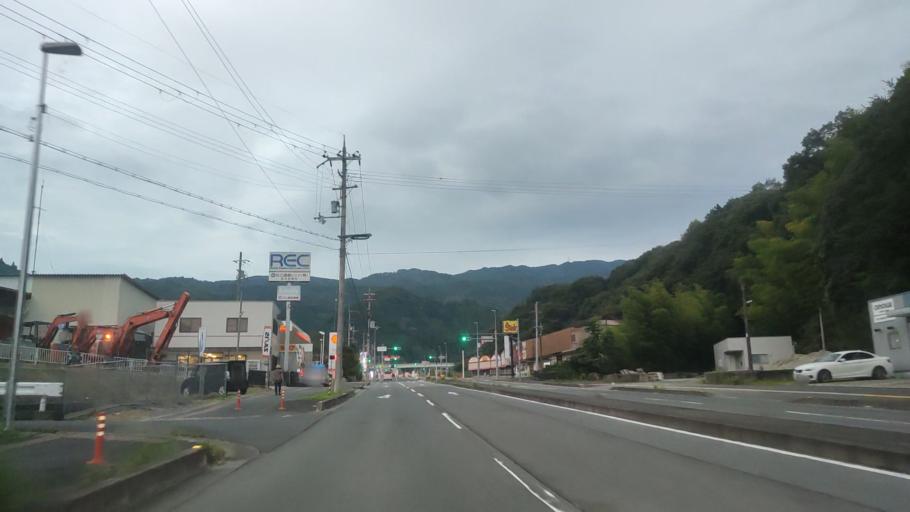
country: JP
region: Wakayama
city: Hashimoto
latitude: 34.3650
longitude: 135.6061
